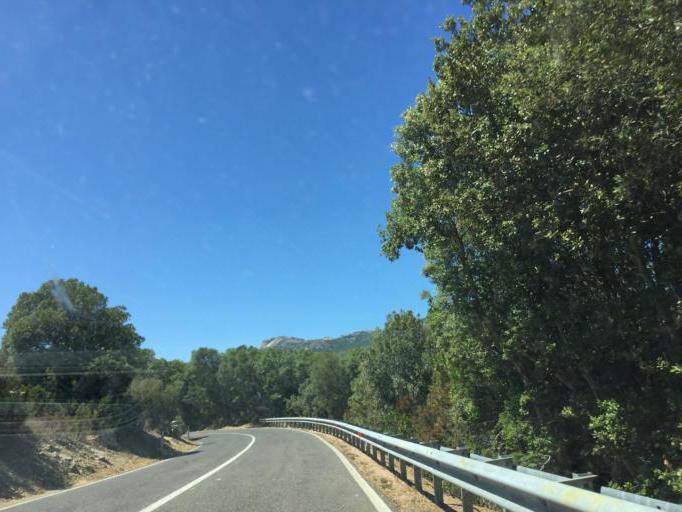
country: IT
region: Sardinia
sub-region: Provincia di Olbia-Tempio
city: Calangianus
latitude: 40.8851
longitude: 9.2508
